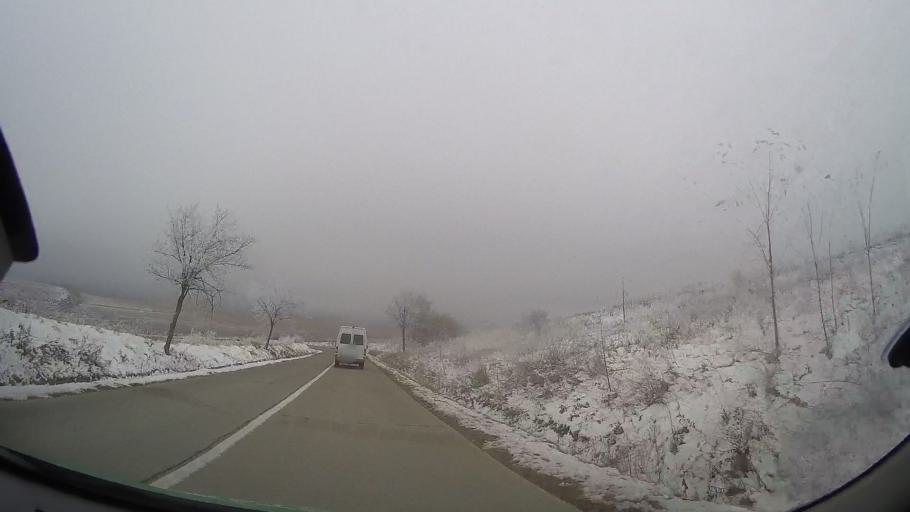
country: RO
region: Vaslui
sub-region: Comuna Grivita
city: Grivita
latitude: 46.1947
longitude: 27.6024
